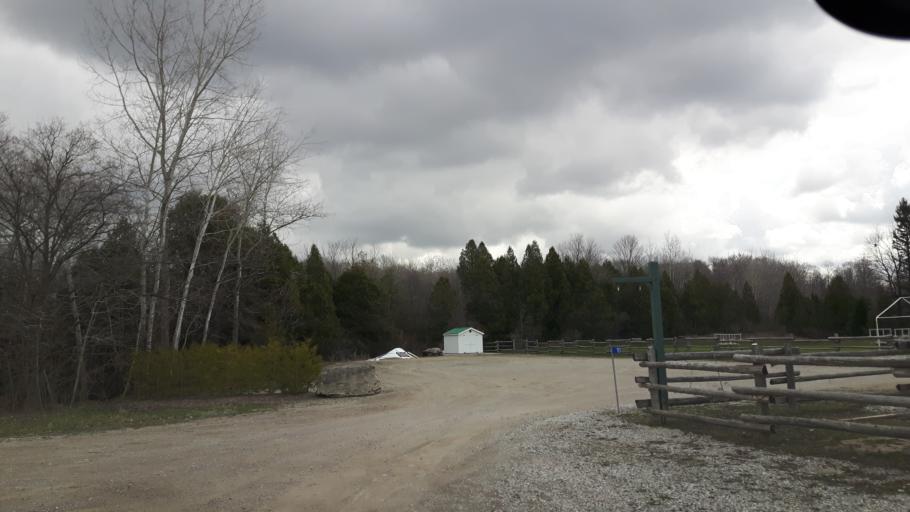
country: CA
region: Ontario
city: Bluewater
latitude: 43.5603
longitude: -81.6837
